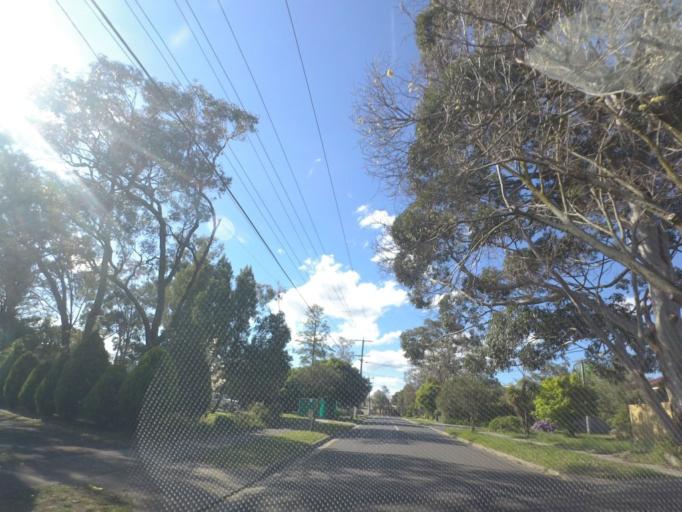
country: AU
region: Victoria
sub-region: Knox
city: Knoxfield
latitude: -37.8871
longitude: 145.2491
